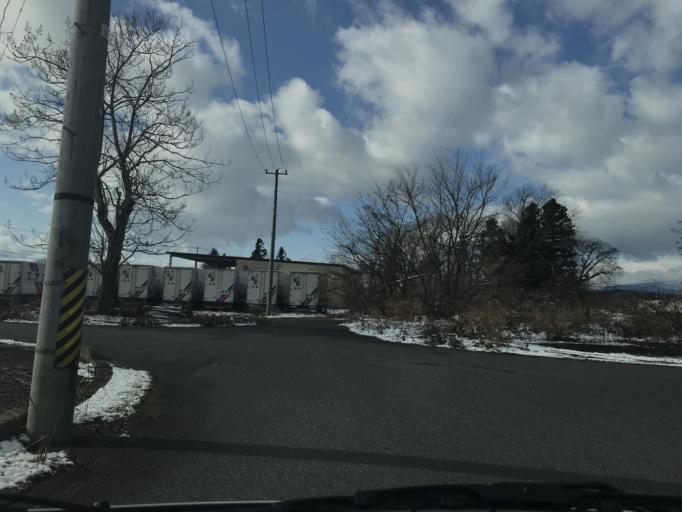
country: JP
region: Iwate
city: Mizusawa
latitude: 39.1635
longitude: 141.0913
